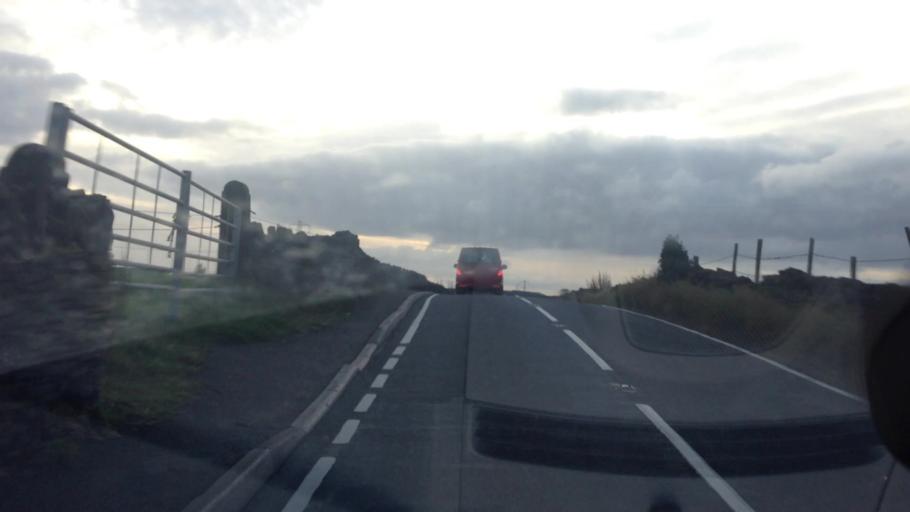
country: GB
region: England
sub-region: Kirklees
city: Mirfield
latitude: 53.6621
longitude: -1.7182
